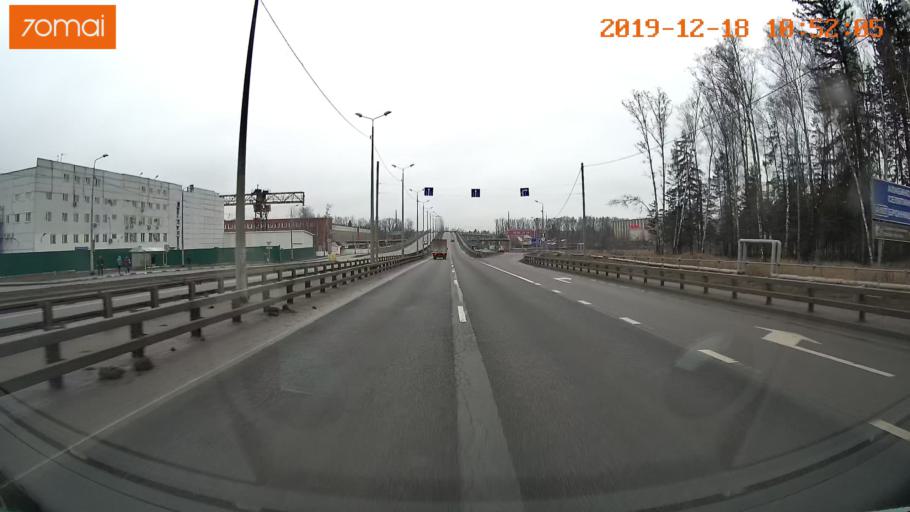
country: RU
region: Moskovskaya
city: Selyatino
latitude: 55.5211
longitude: 36.9870
